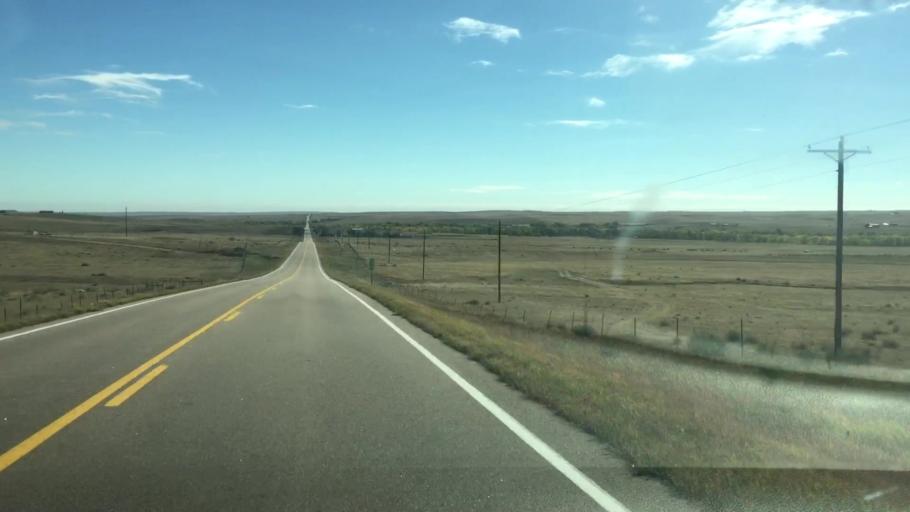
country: US
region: Colorado
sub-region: Elbert County
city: Kiowa
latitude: 39.2735
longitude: -104.1708
